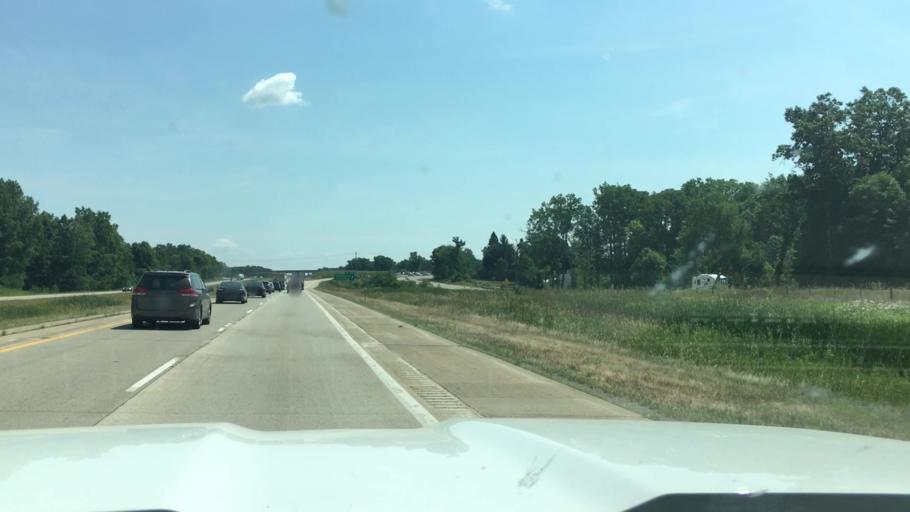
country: US
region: Michigan
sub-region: Ingham County
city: Haslett
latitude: 42.7965
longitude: -84.3618
